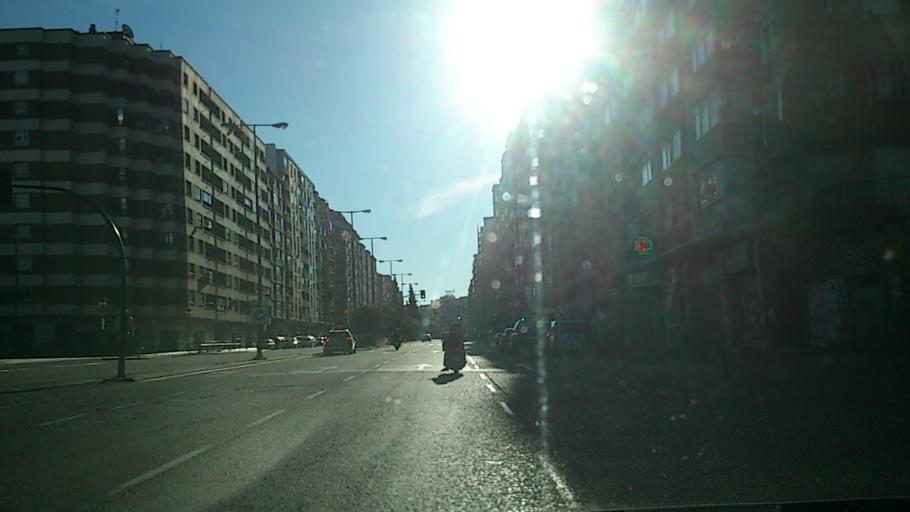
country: ES
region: Aragon
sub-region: Provincia de Zaragoza
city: Delicias
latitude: 41.6555
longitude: -0.9072
